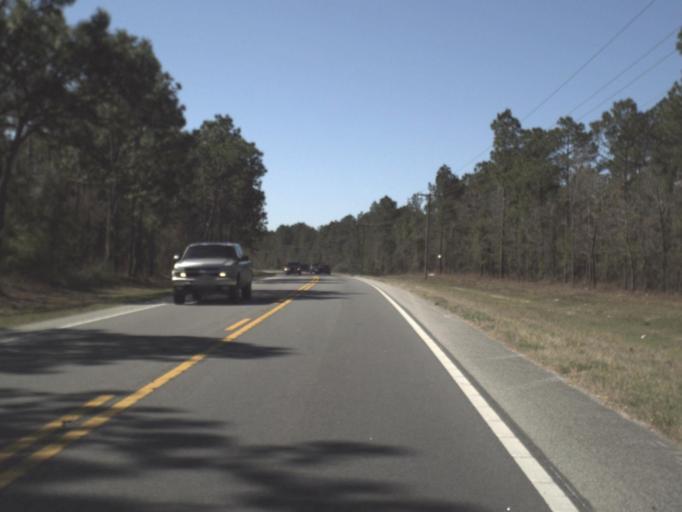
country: US
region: Florida
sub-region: Leon County
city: Woodville
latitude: 30.3148
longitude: -84.3405
